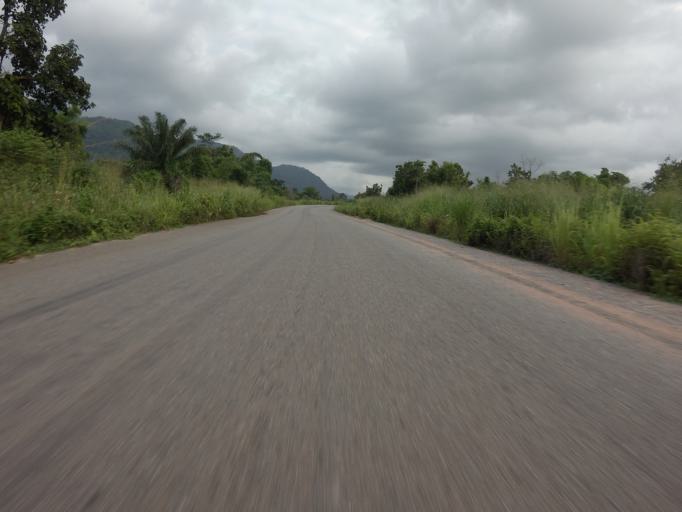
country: GH
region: Volta
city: Kpandu
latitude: 6.8246
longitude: 0.3786
